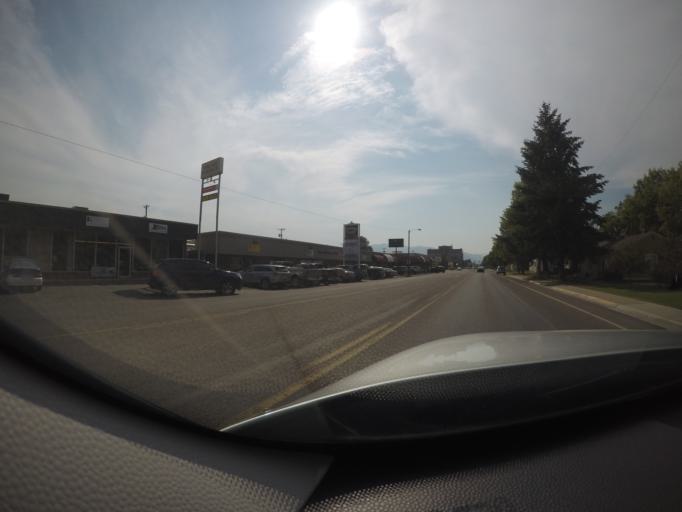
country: US
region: Montana
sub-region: Missoula County
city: Orchard Homes
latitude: 46.8489
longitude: -114.0208
